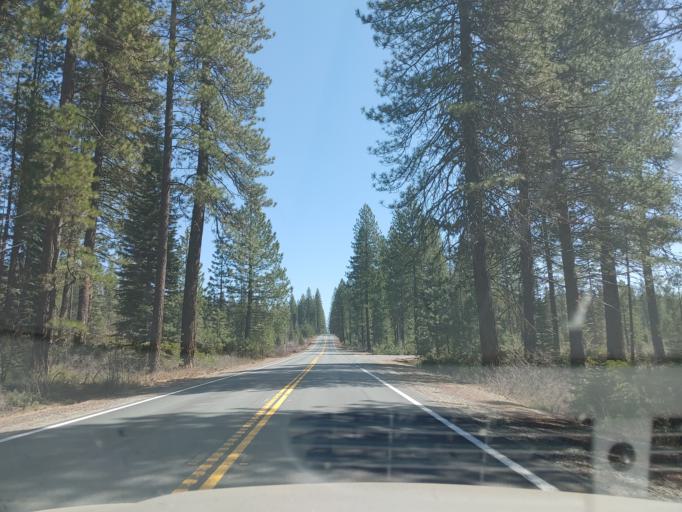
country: US
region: California
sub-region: Siskiyou County
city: McCloud
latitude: 41.2665
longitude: -121.8803
